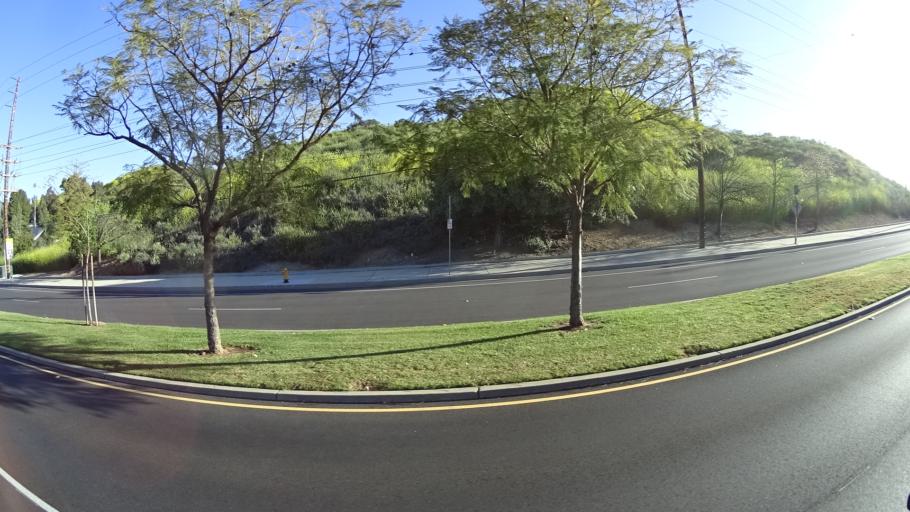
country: US
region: California
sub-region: Los Angeles County
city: Westlake Village
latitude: 34.1567
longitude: -118.8113
